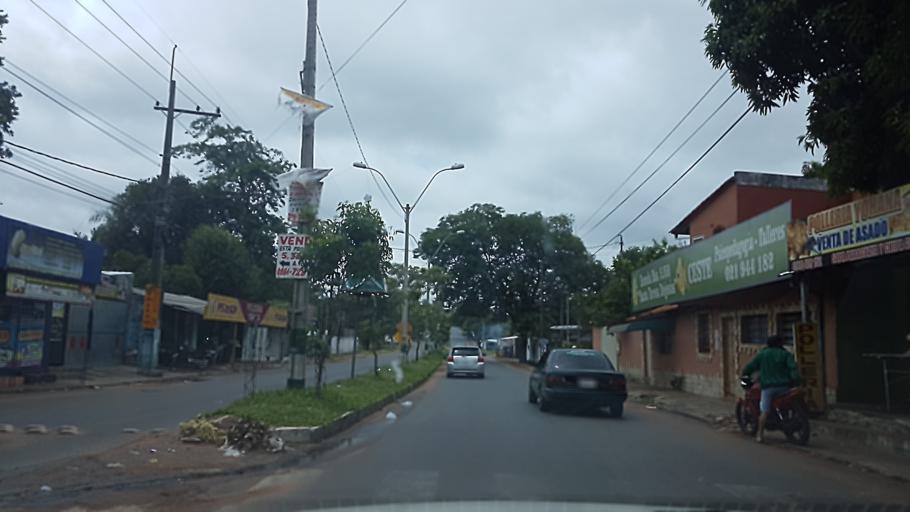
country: PY
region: Central
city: Villa Elisa
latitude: -25.3922
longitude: -57.5824
